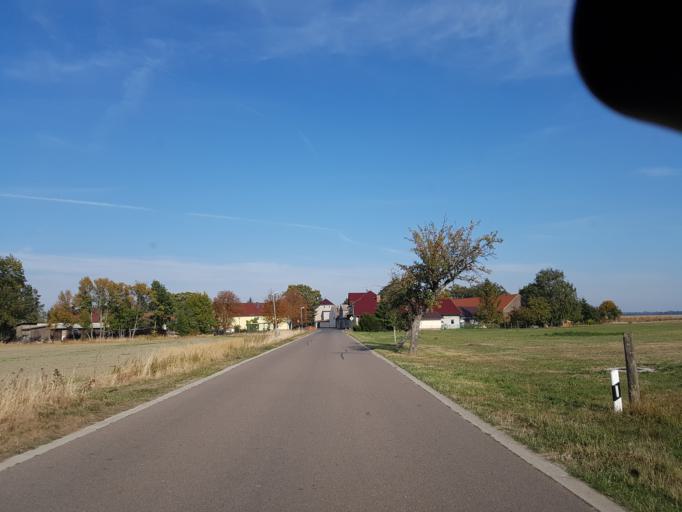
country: DE
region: Brandenburg
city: Doberlug-Kirchhain
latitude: 51.6682
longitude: 13.5100
